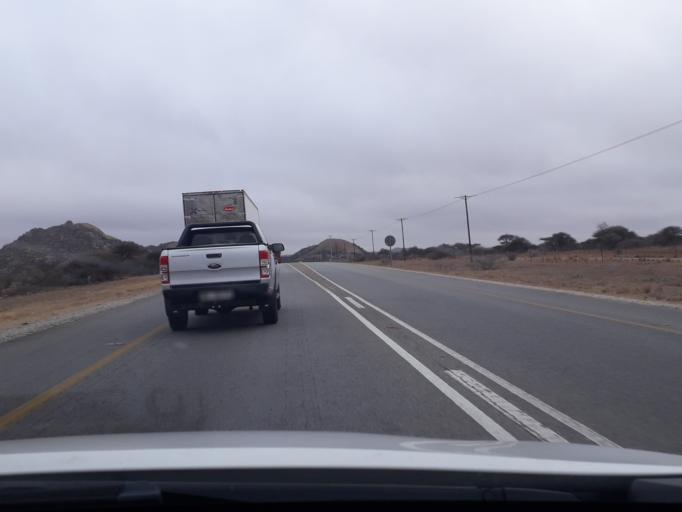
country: ZA
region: Limpopo
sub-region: Capricorn District Municipality
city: Mankoeng
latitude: -23.5410
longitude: 29.6973
